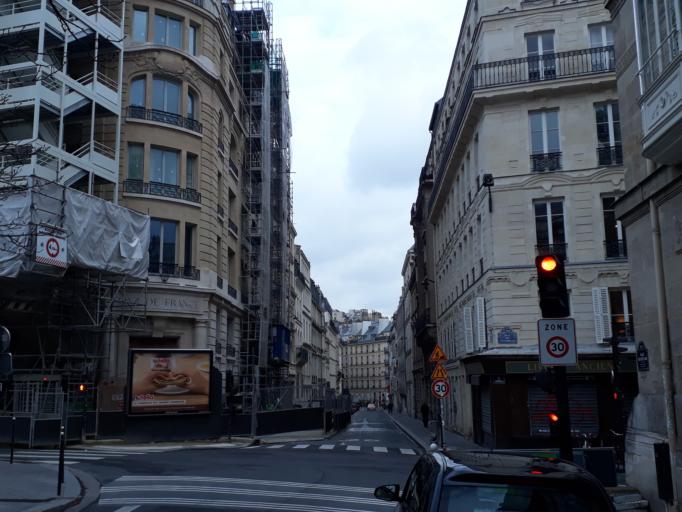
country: FR
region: Ile-de-France
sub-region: Paris
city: Saint-Ouen
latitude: 48.8829
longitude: 2.3297
